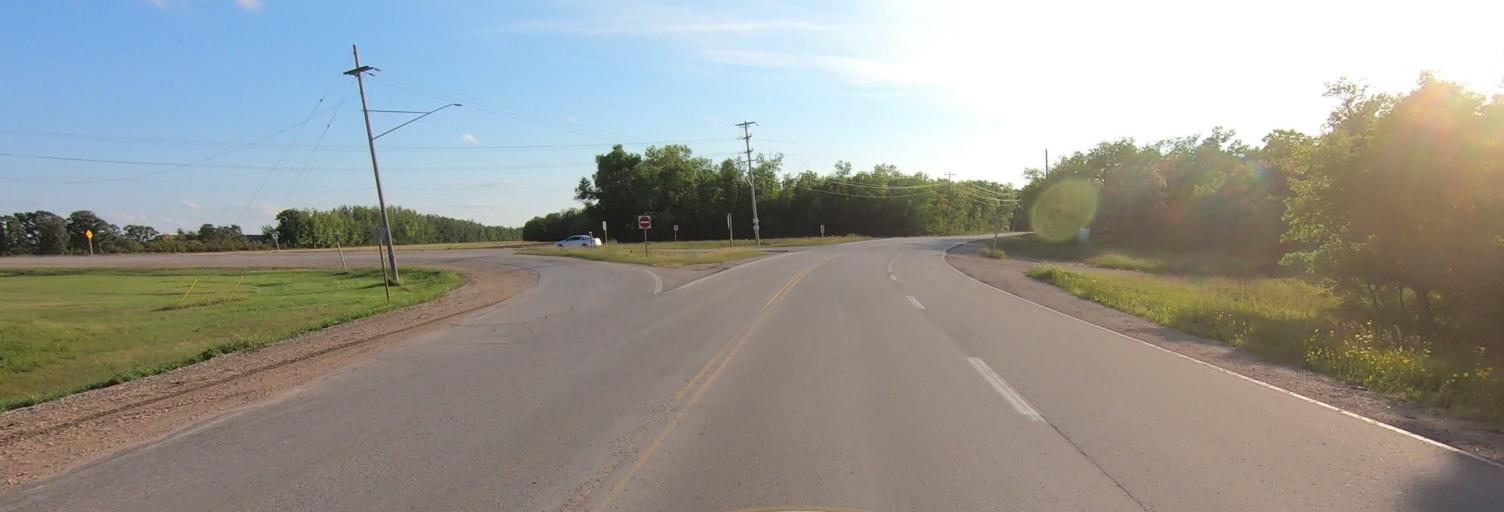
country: CA
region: Manitoba
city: Selkirk
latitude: 50.1233
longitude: -96.8589
